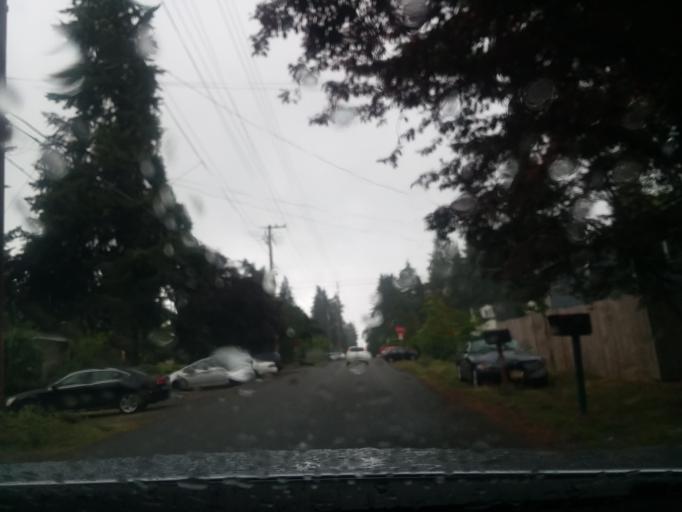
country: US
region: Washington
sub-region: King County
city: Shoreline
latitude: 47.7190
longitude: -122.3209
